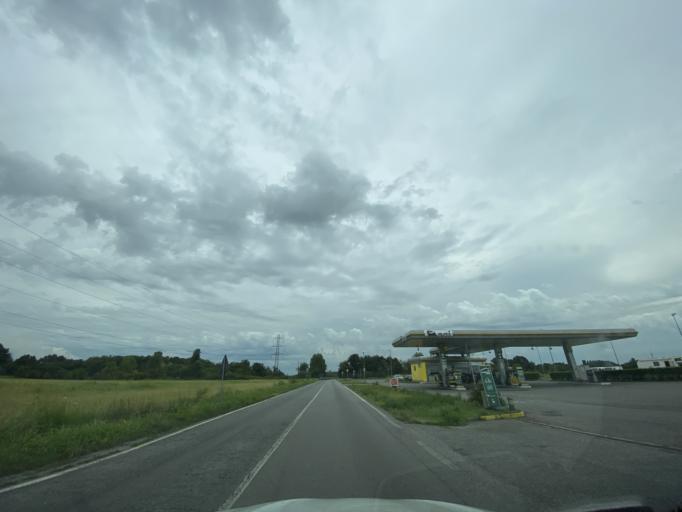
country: IT
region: Lombardy
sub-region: Provincia di Monza e Brianza
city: Caponago
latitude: 45.5603
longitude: 9.3762
